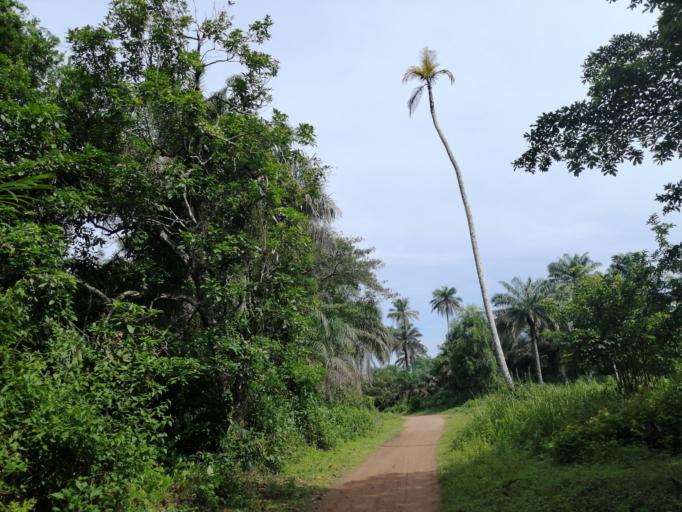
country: SL
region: Northern Province
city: Port Loko
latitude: 8.7888
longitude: -12.9267
